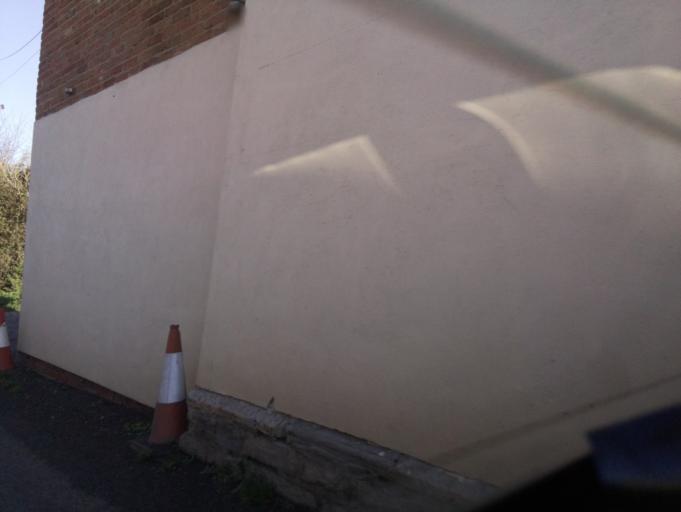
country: GB
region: England
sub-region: Somerset
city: Martock
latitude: 51.0100
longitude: -2.7613
